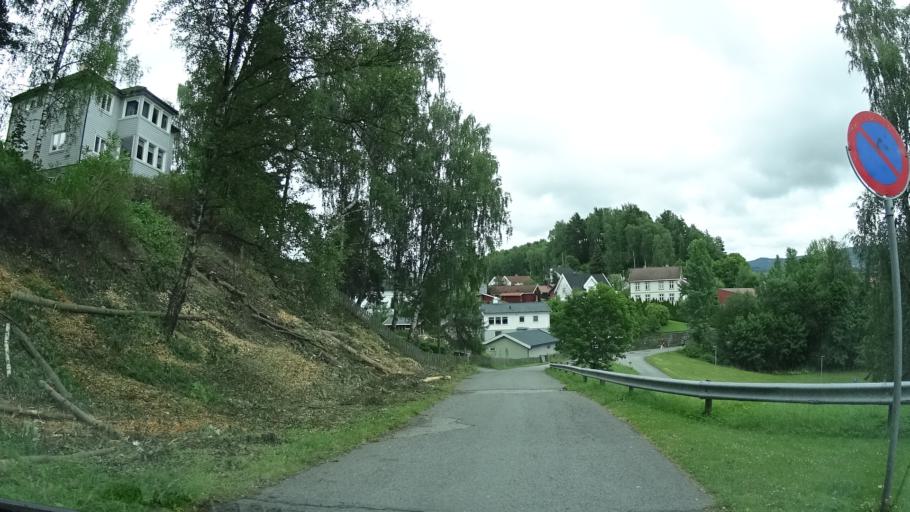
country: NO
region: Buskerud
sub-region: Ringerike
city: Honefoss
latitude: 60.1704
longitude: 10.2540
